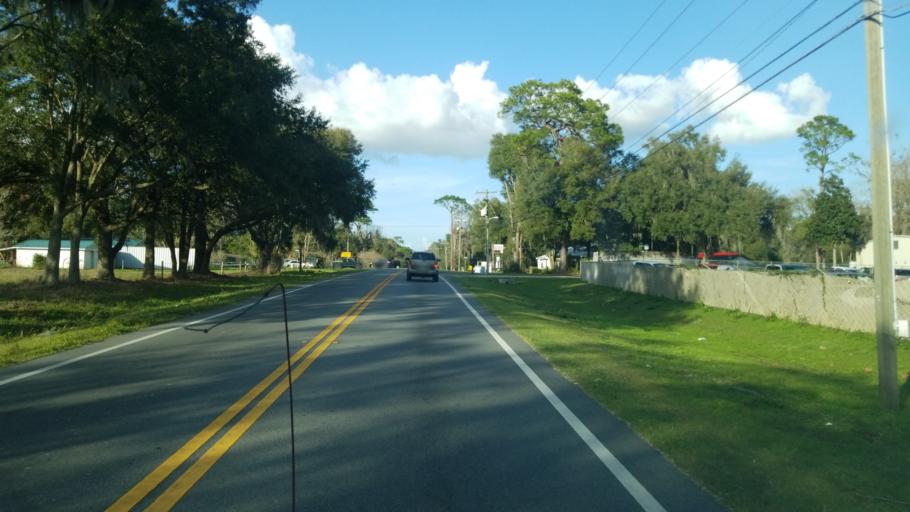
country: US
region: Florida
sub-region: Marion County
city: Ocala
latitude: 29.2291
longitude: -82.1222
